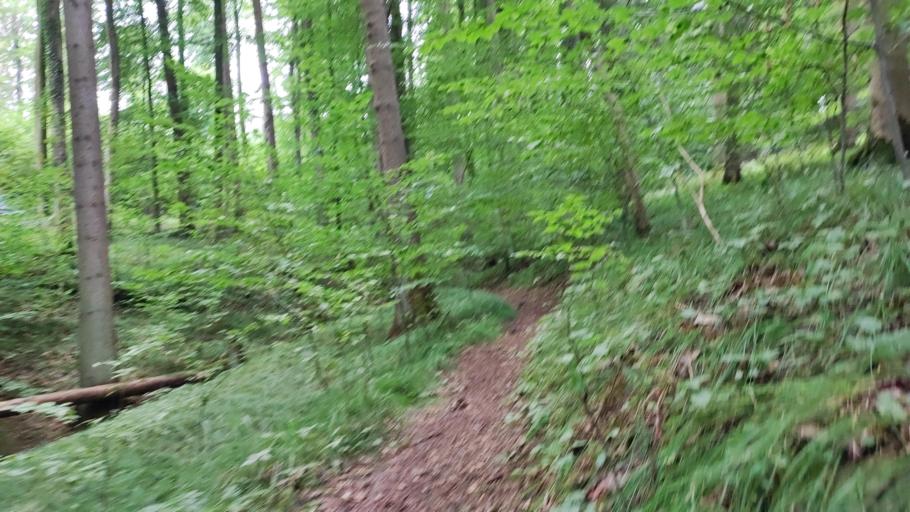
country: DE
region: Bavaria
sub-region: Swabia
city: Jettingen-Scheppach
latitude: 48.3711
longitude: 10.4012
